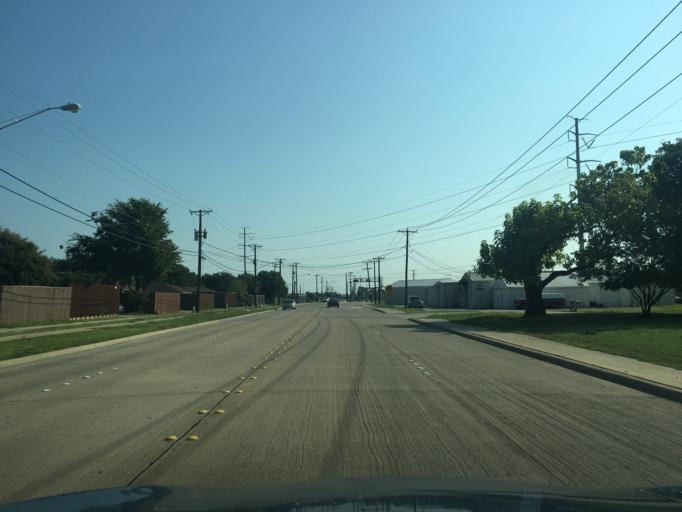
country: US
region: Texas
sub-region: Dallas County
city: Garland
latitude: 32.9382
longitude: -96.6249
